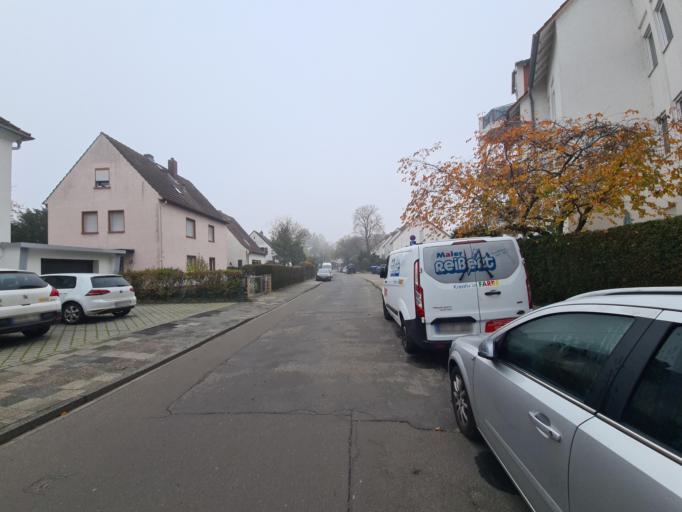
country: DE
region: Rheinland-Pfalz
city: Worms
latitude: 49.6369
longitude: 8.3393
